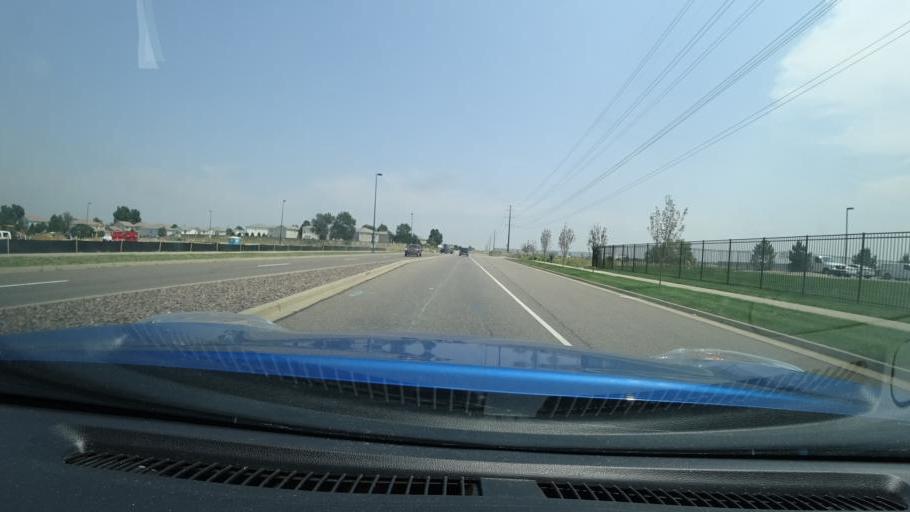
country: US
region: Colorado
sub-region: Adams County
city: Aurora
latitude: 39.7693
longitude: -104.7548
